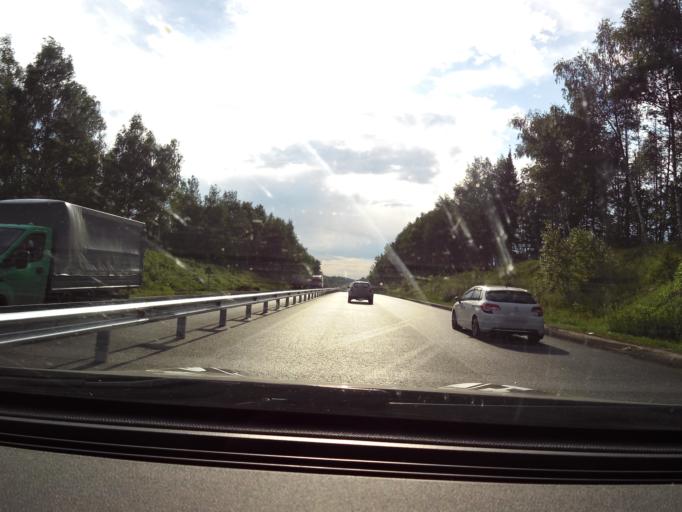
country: RU
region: Vladimir
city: Novovyazniki
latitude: 56.2030
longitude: 42.3388
